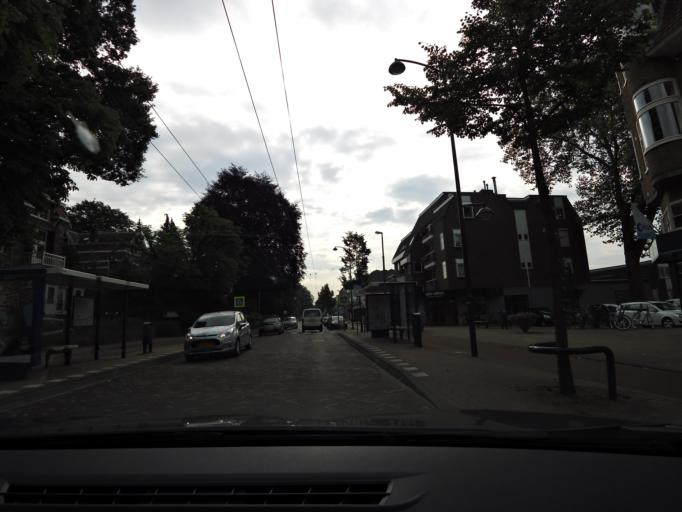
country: NL
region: Gelderland
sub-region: Gemeente Renkum
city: Oosterbeek
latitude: 51.9869
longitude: 5.8458
